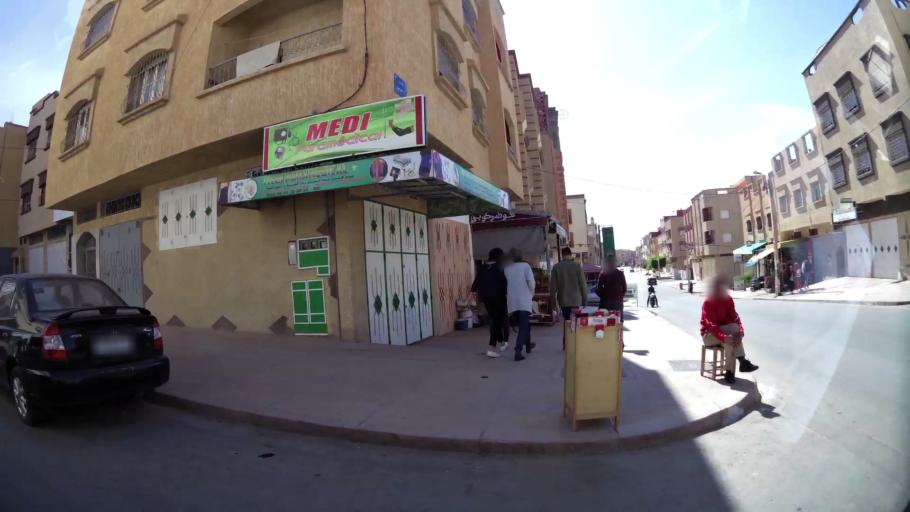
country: MA
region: Oriental
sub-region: Oujda-Angad
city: Oujda
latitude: 34.6576
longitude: -1.9142
